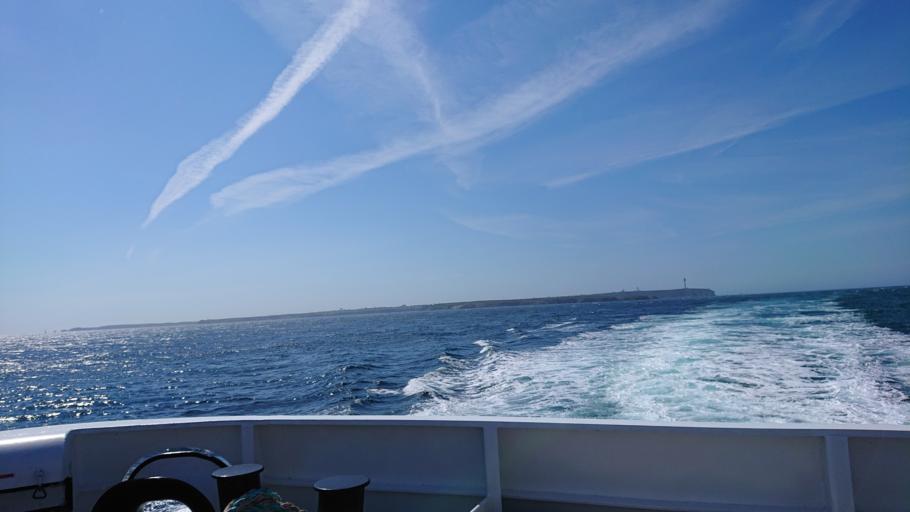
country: FR
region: Brittany
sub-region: Departement du Finistere
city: Porspoder
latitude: 48.4509
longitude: -5.0068
